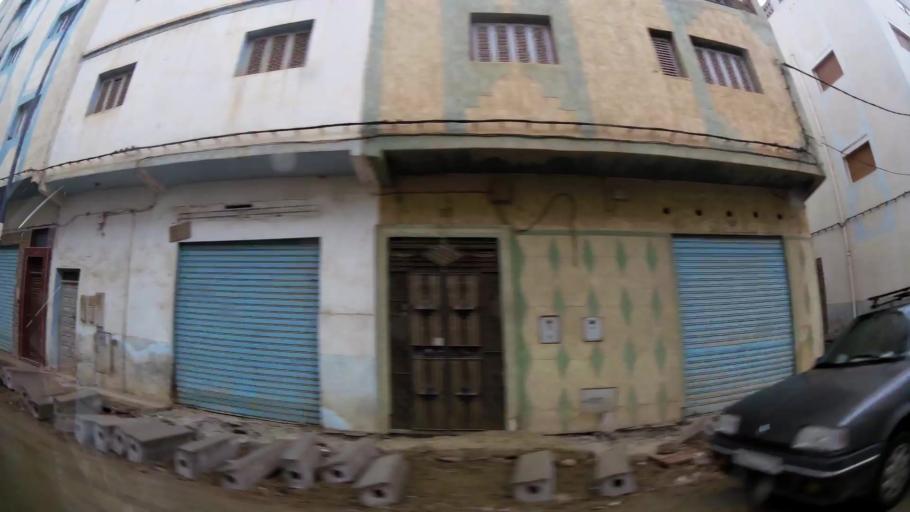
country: MA
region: Taza-Al Hoceima-Taounate
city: Imzourene
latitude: 35.1511
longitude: -3.8452
